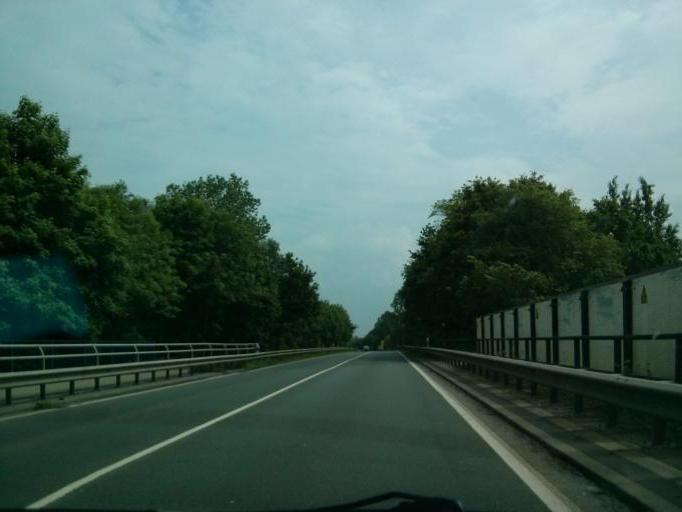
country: DE
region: Lower Saxony
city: Loxstedt
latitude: 53.4946
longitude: 8.6341
